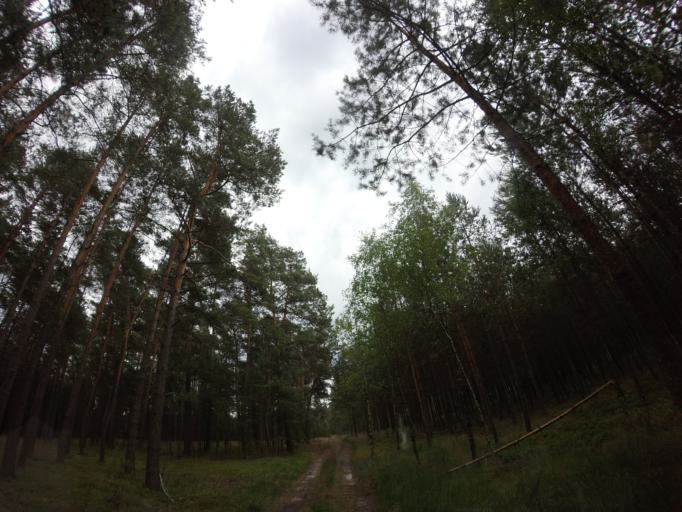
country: PL
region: West Pomeranian Voivodeship
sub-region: Powiat choszczenski
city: Drawno
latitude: 53.1541
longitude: 15.7477
